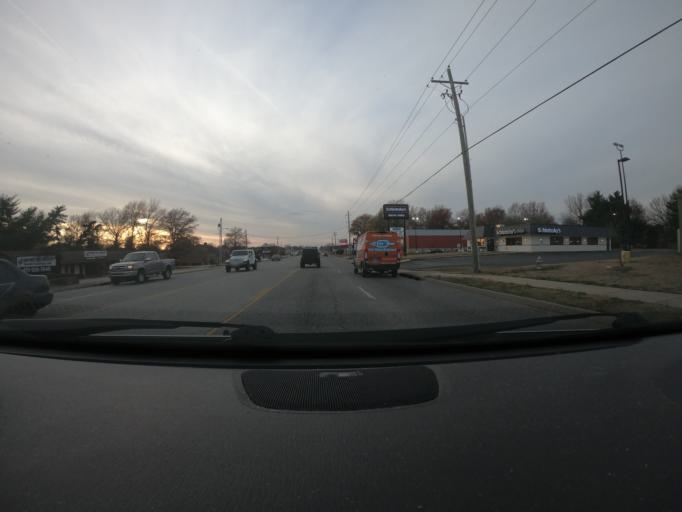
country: US
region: Arkansas
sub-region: Benton County
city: Rogers
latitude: 36.3343
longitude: -94.1537
